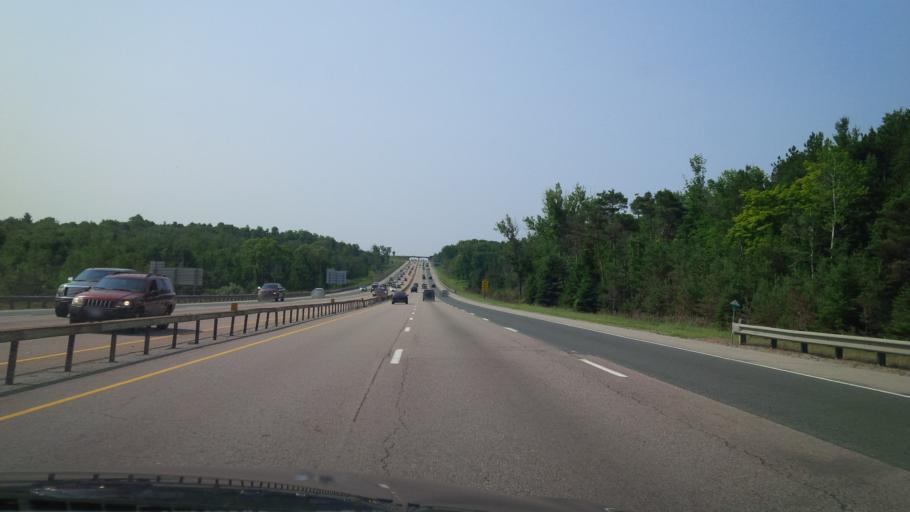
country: CA
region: Ontario
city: Innisfil
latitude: 44.3210
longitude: -79.6830
